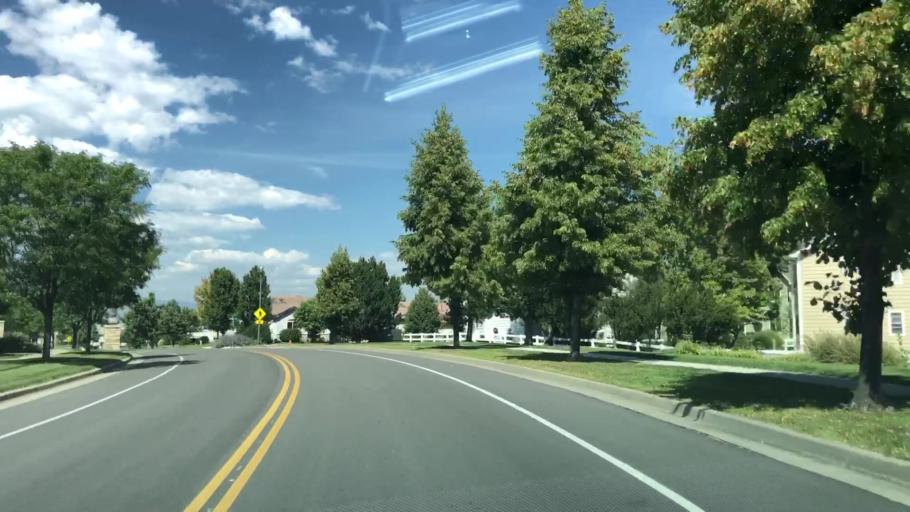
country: US
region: Colorado
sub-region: Larimer County
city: Loveland
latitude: 40.3948
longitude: -105.1409
